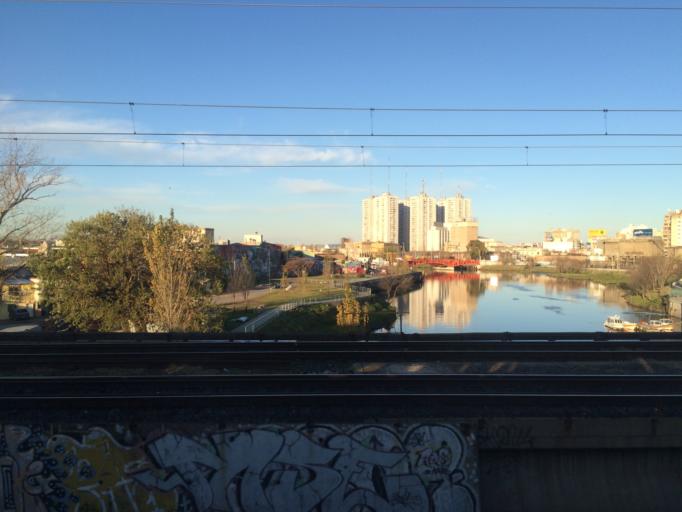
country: AR
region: Buenos Aires
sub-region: Partido de Avellaneda
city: Avellaneda
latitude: -34.6572
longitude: -58.3779
